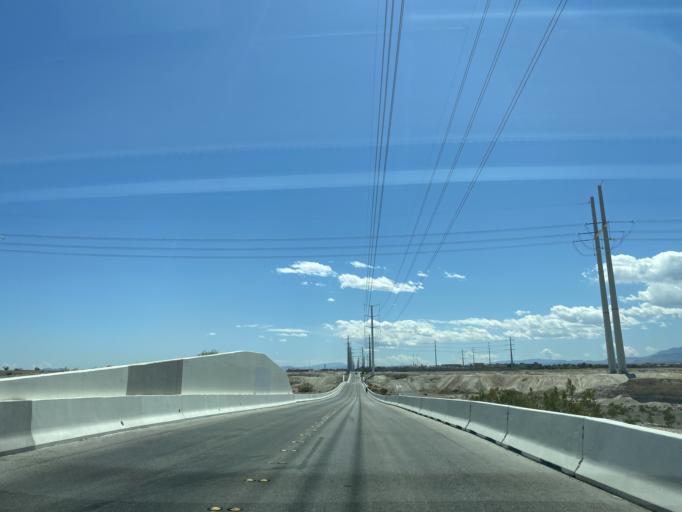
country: US
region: Nevada
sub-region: Clark County
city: North Las Vegas
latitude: 36.3294
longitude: -115.2071
